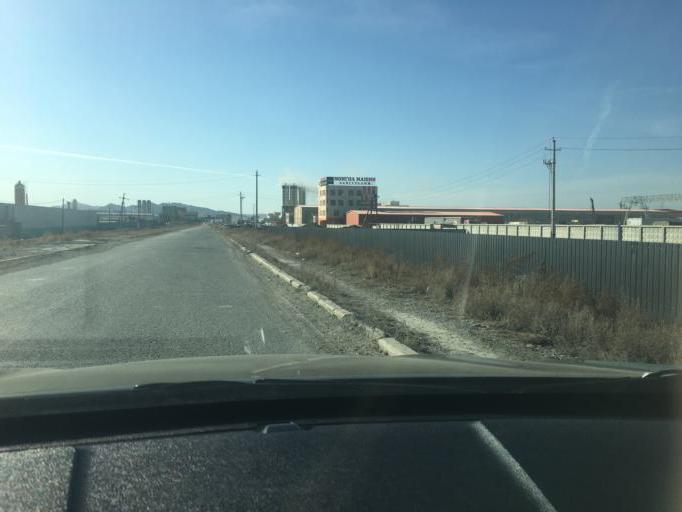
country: MN
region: Ulaanbaatar
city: Ulaanbaatar
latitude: 47.8882
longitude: 106.7830
